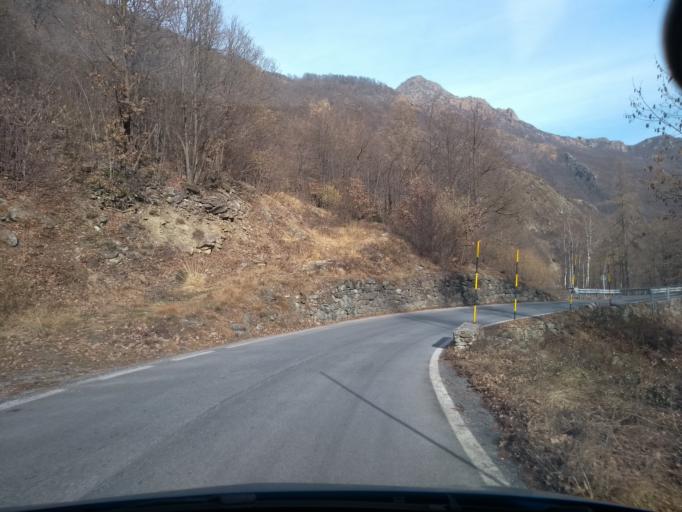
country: IT
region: Piedmont
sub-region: Provincia di Torino
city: Ala di Stura
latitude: 45.3170
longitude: 7.3318
